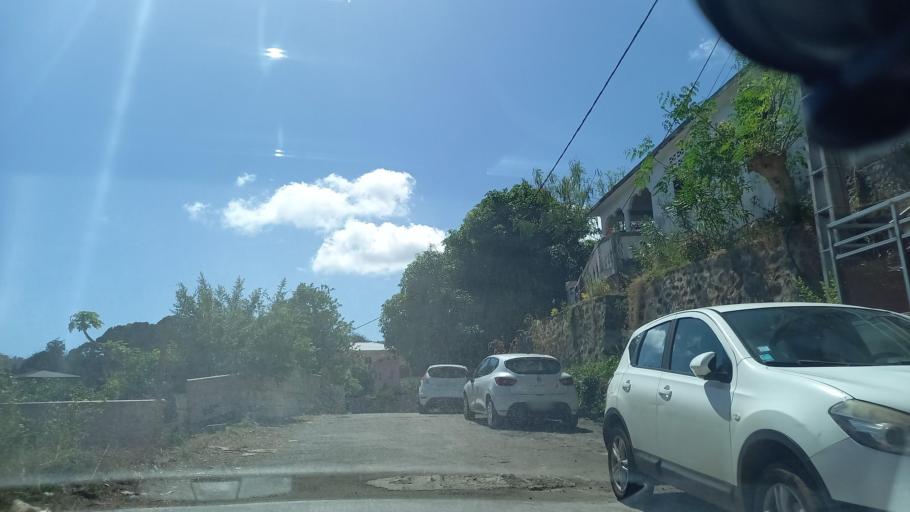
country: YT
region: Kani-Keli
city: Kani Keli
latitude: -12.9656
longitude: 45.1130
